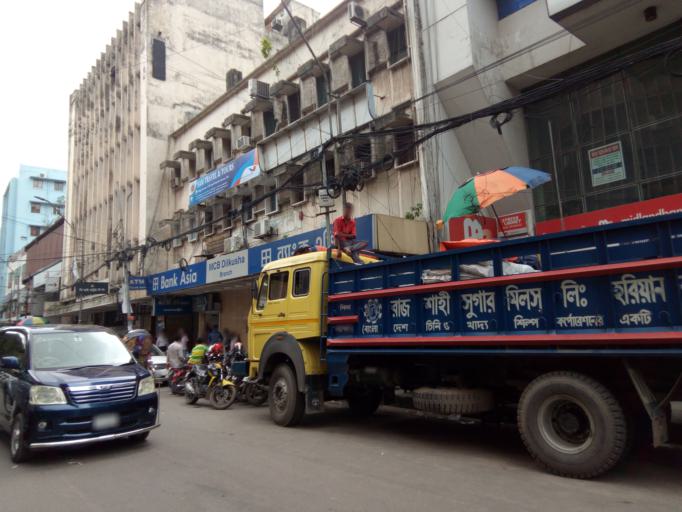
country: BD
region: Dhaka
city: Paltan
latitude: 23.7278
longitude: 90.4174
